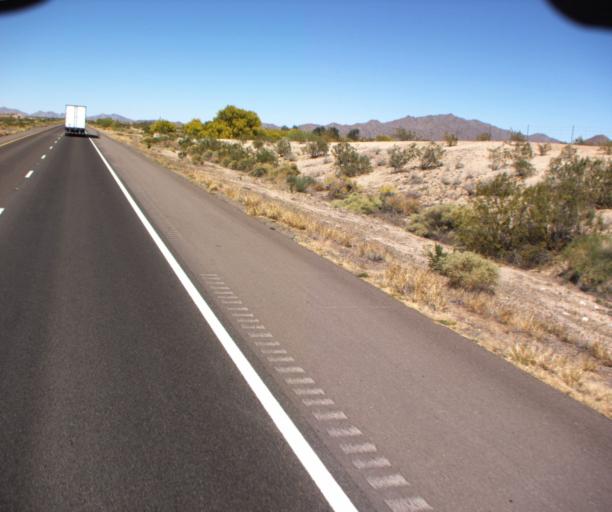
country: US
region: Arizona
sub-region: Maricopa County
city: Gila Bend
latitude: 33.0921
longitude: -112.6483
